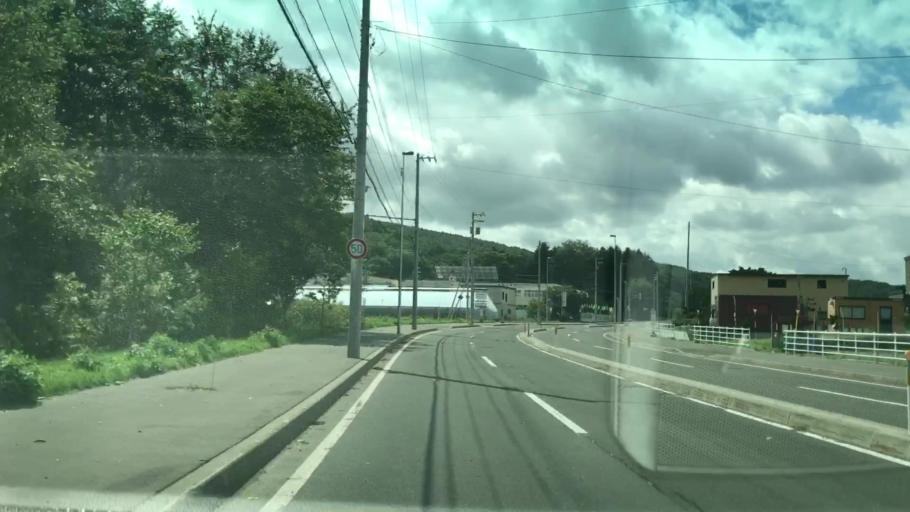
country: JP
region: Hokkaido
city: Kitahiroshima
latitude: 42.9522
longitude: 141.4514
